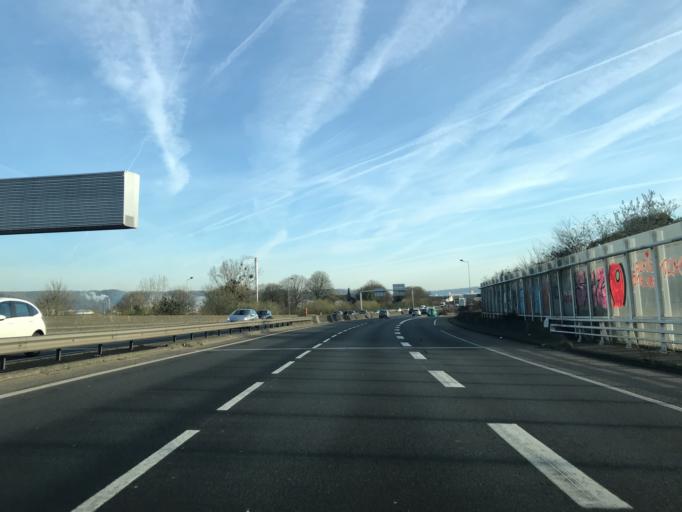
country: FR
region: Haute-Normandie
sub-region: Departement de la Seine-Maritime
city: Le Grand-Quevilly
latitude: 49.3991
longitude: 1.0319
